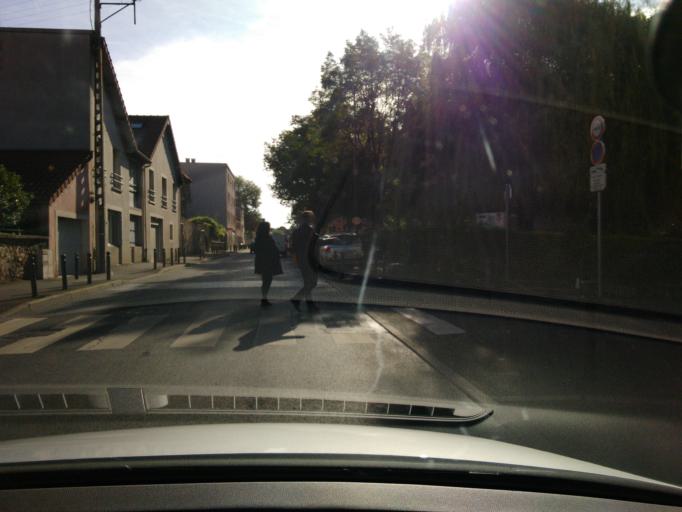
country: FR
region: Ile-de-France
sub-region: Departement de l'Essonne
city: Massy
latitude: 48.7291
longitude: 2.2765
